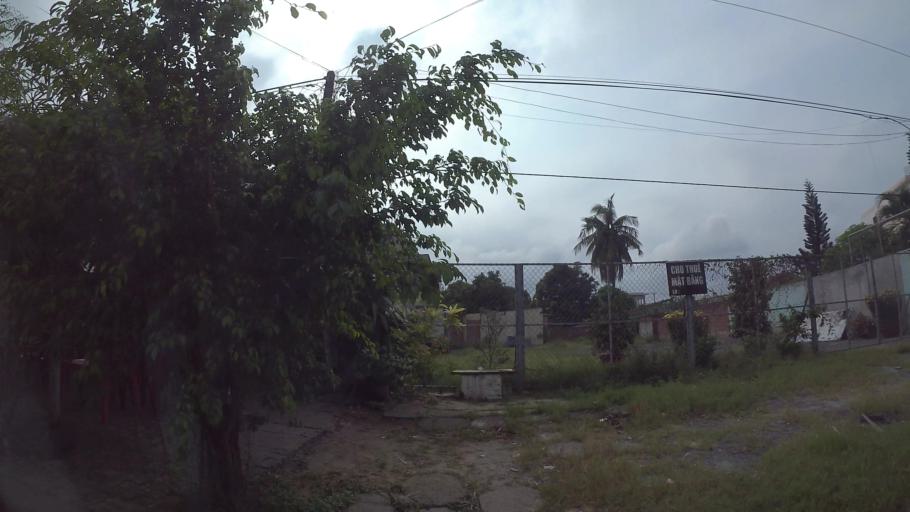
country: VN
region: Da Nang
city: Son Tra
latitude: 16.0723
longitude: 108.2398
